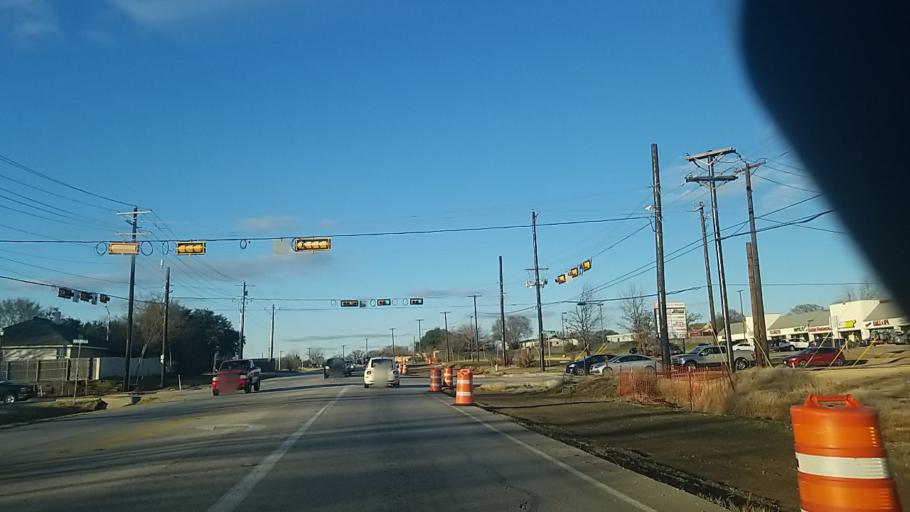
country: US
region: Texas
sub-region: Denton County
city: Corinth
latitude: 33.1579
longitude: -97.1056
